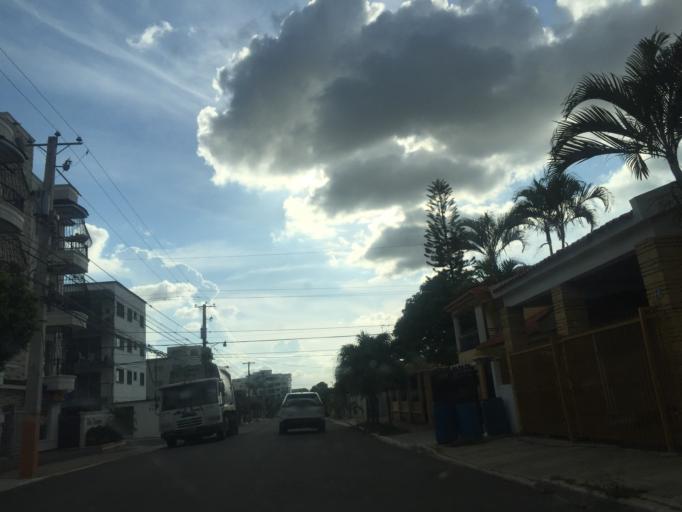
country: DO
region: Santiago
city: Santiago de los Caballeros
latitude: 19.4346
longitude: -70.6639
